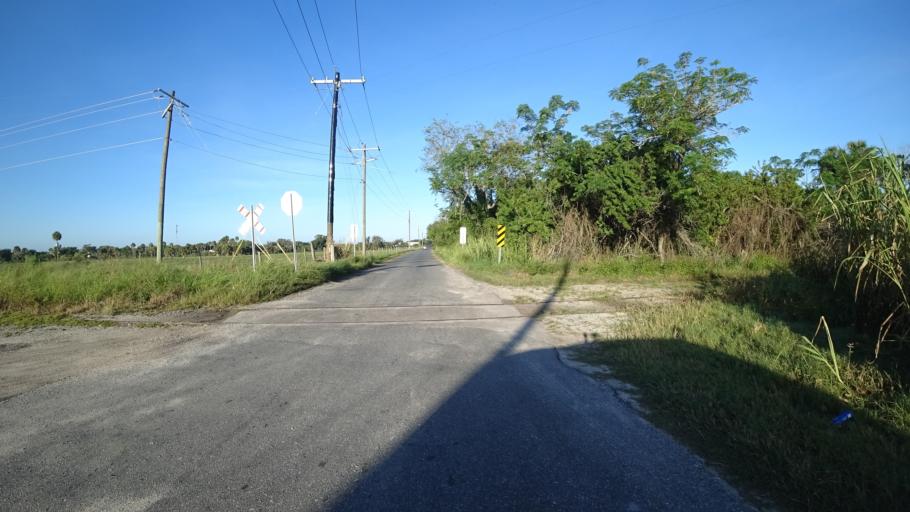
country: US
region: Florida
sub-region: Manatee County
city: Ellenton
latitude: 27.5328
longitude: -82.5357
